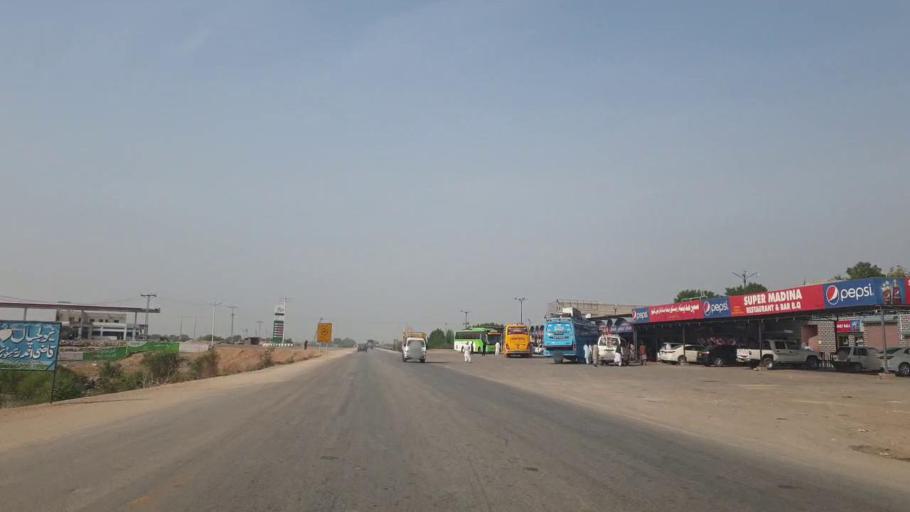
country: PK
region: Sindh
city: Sann
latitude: 26.1594
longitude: 68.0216
